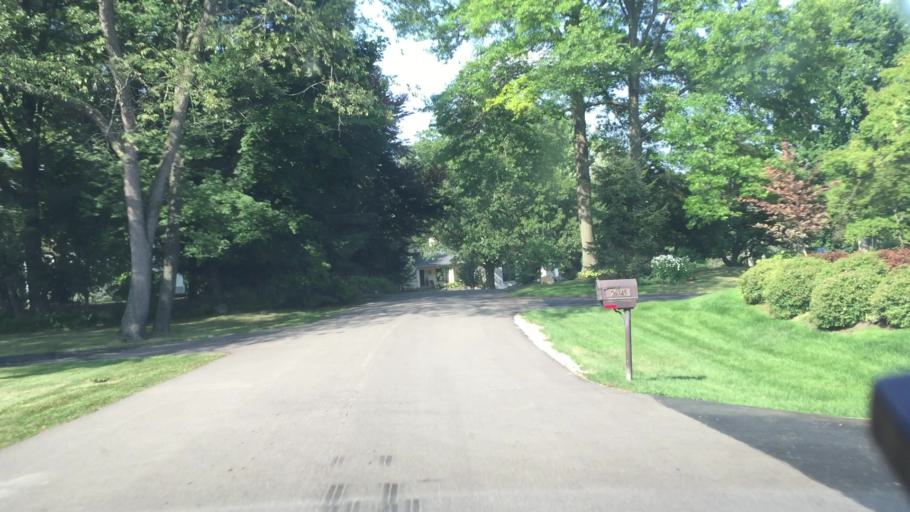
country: US
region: Michigan
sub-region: Oakland County
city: Franklin
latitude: 42.5281
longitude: -83.3087
